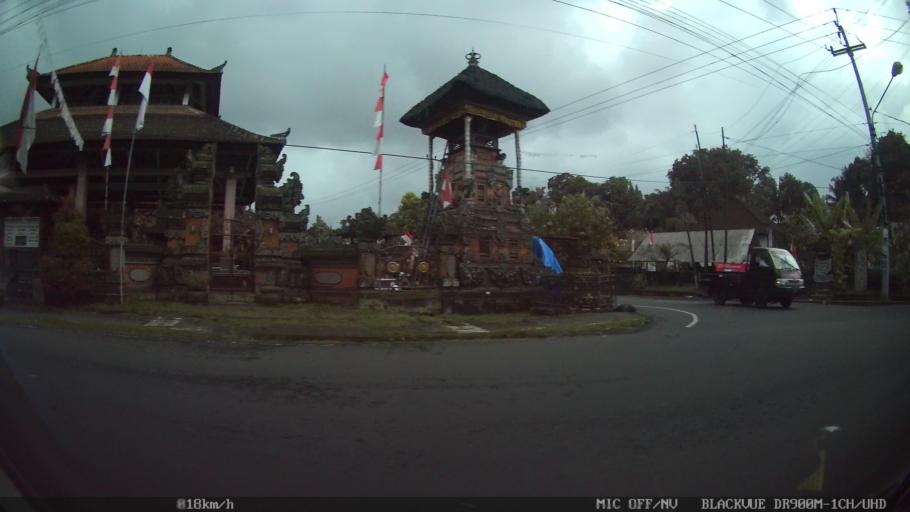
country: ID
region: Bali
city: Banjar Keraman
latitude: -8.5255
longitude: 115.2122
